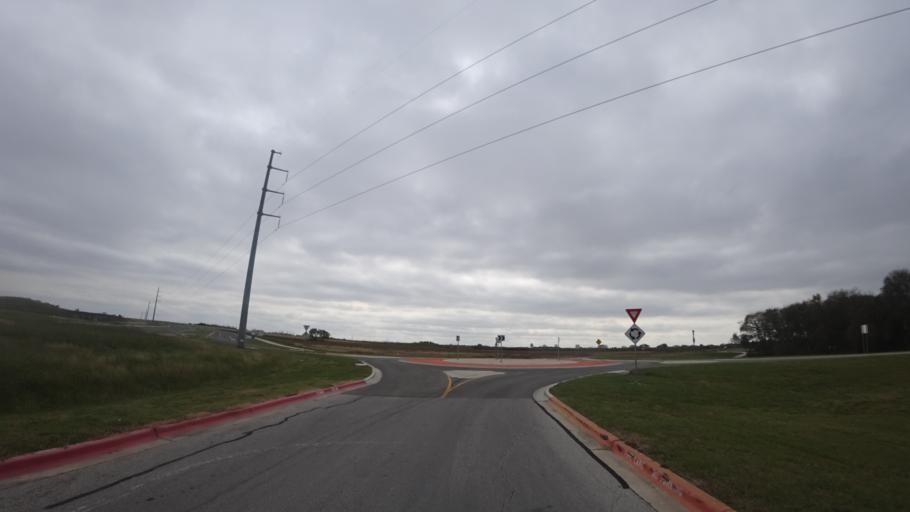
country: US
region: Texas
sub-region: Travis County
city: Pflugerville
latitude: 30.4092
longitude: -97.5976
